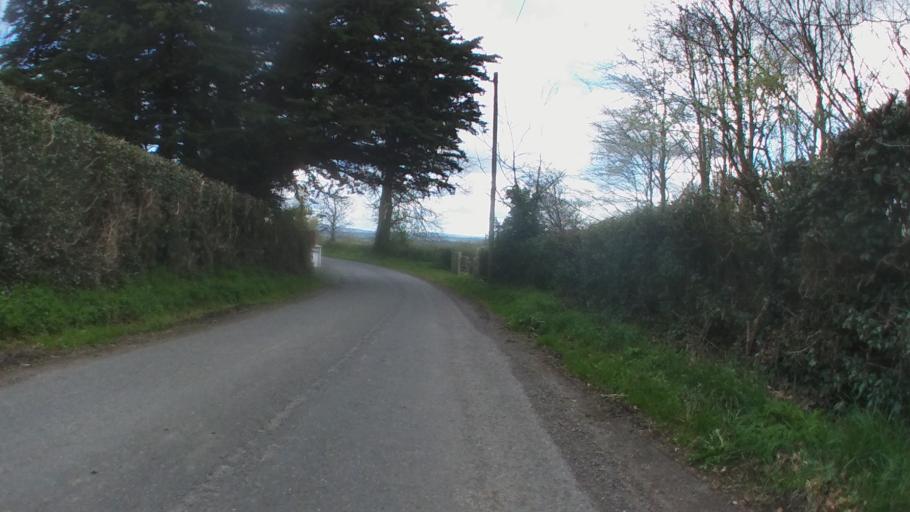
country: IE
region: Leinster
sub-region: Kilkenny
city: Kilkenny
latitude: 52.7097
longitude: -7.2167
